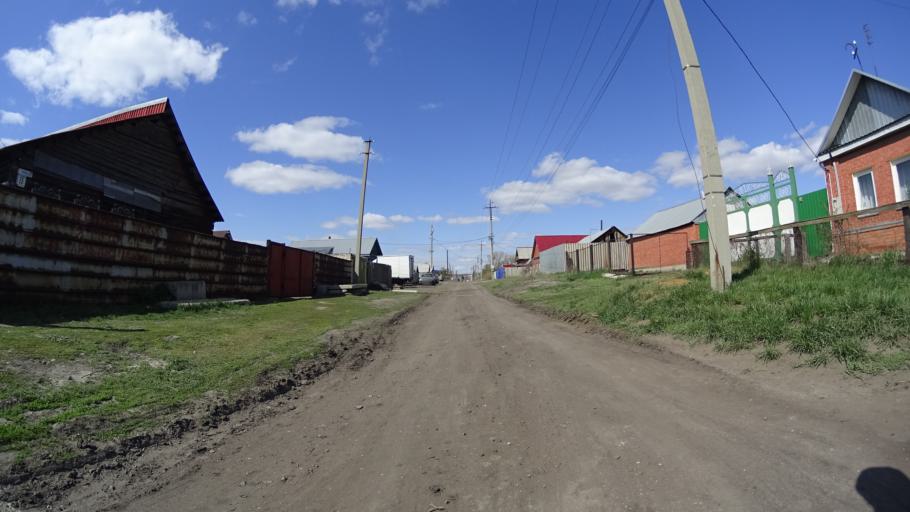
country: RU
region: Chelyabinsk
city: Troitsk
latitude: 54.0874
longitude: 61.5954
